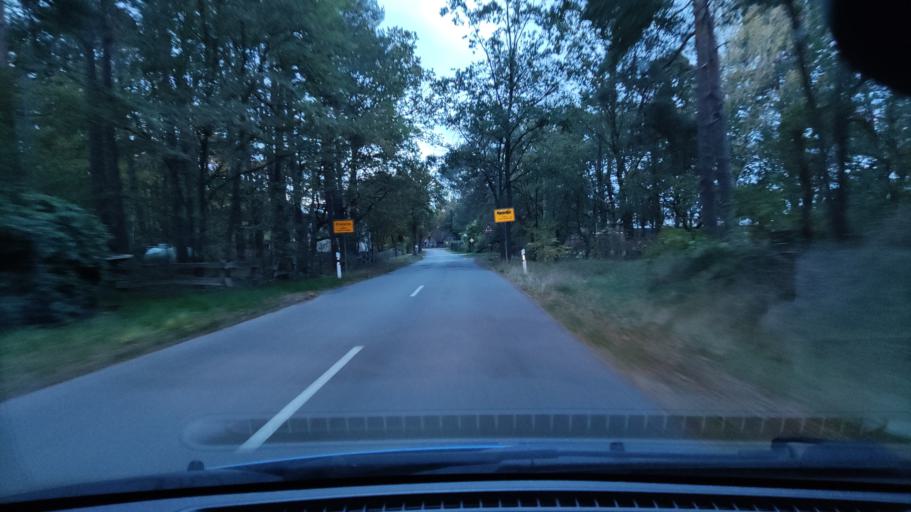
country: DE
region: Lower Saxony
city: Prezelle
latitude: 52.9664
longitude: 11.3997
